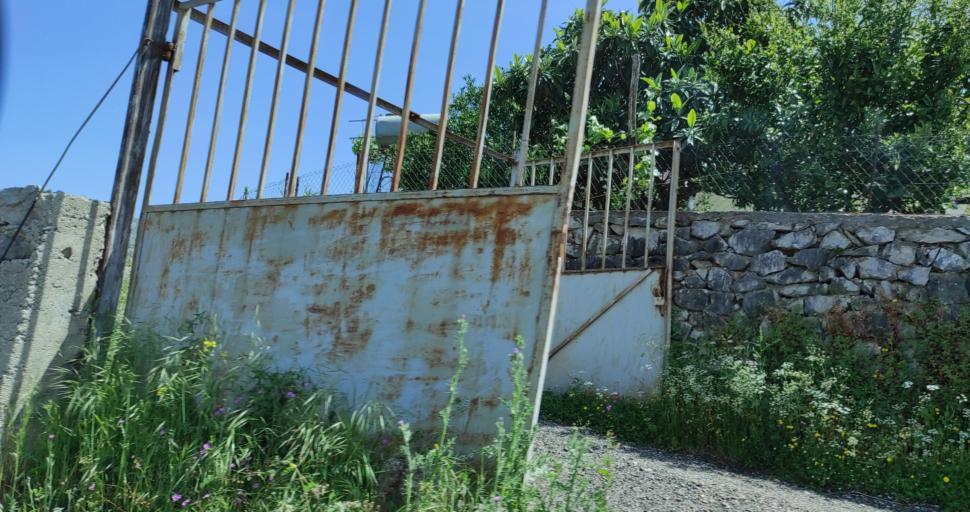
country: AL
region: Shkoder
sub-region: Rrethi i Malesia e Madhe
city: Gruemire
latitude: 42.1205
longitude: 19.5792
